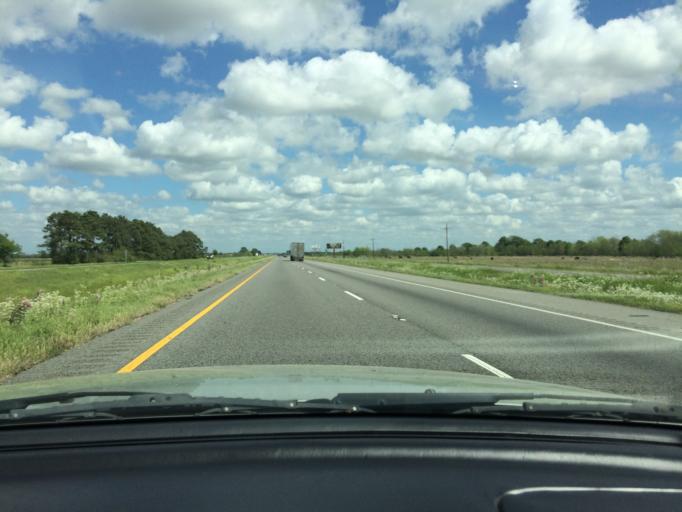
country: US
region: Louisiana
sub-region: Jefferson Davis Parish
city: Jennings
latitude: 30.2466
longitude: -92.7157
